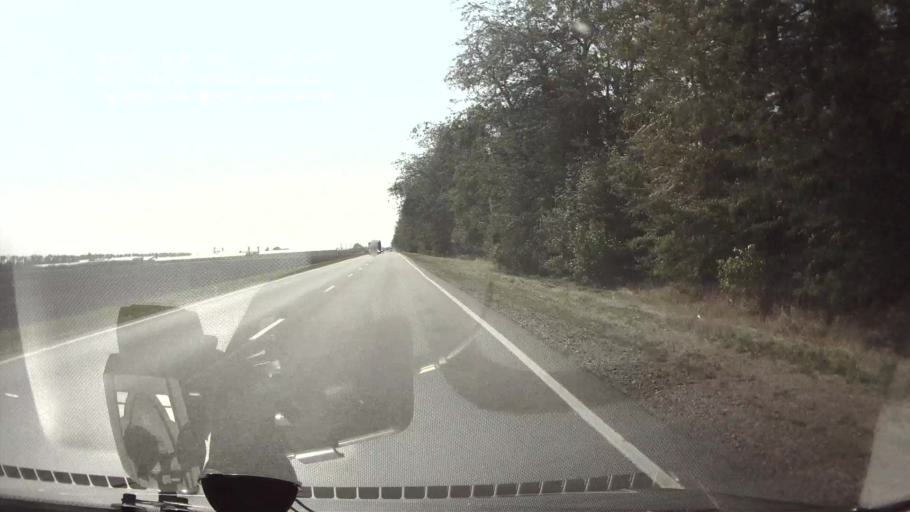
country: RU
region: Krasnodarskiy
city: Kavkazskaya
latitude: 45.4882
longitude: 40.6804
